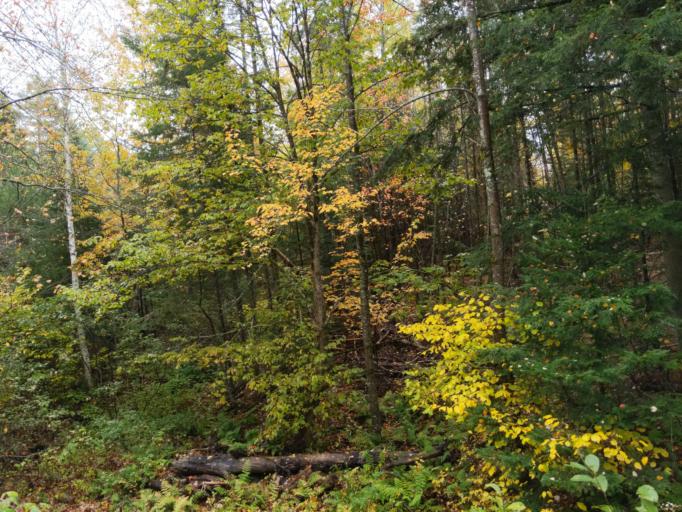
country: US
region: Maine
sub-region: Lincoln County
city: Whitefield
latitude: 44.0976
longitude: -69.6234
